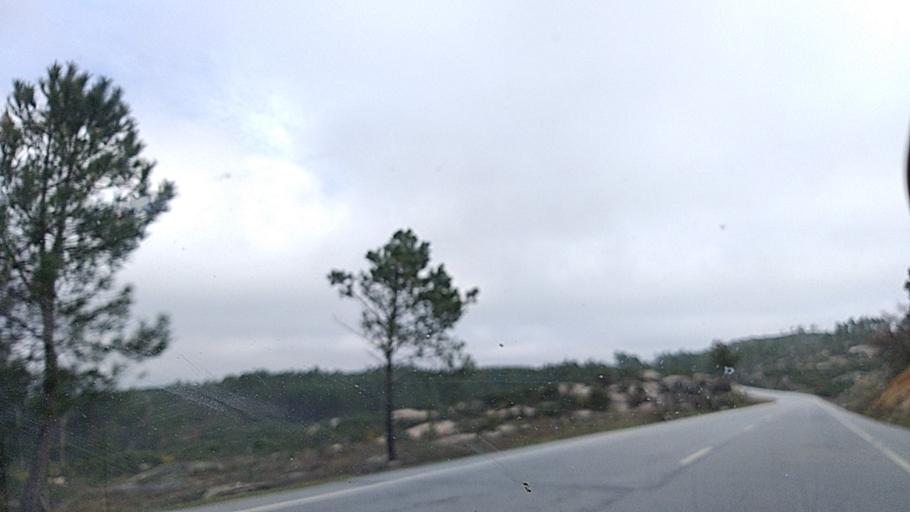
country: PT
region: Guarda
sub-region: Aguiar da Beira
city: Aguiar da Beira
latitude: 40.7555
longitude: -7.5040
